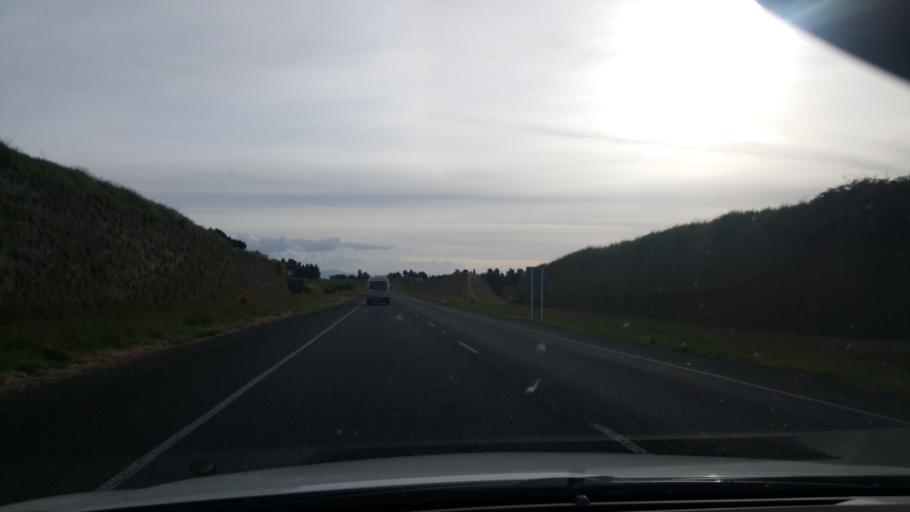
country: NZ
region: Waikato
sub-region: Taupo District
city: Taupo
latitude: -38.7322
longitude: 176.0818
